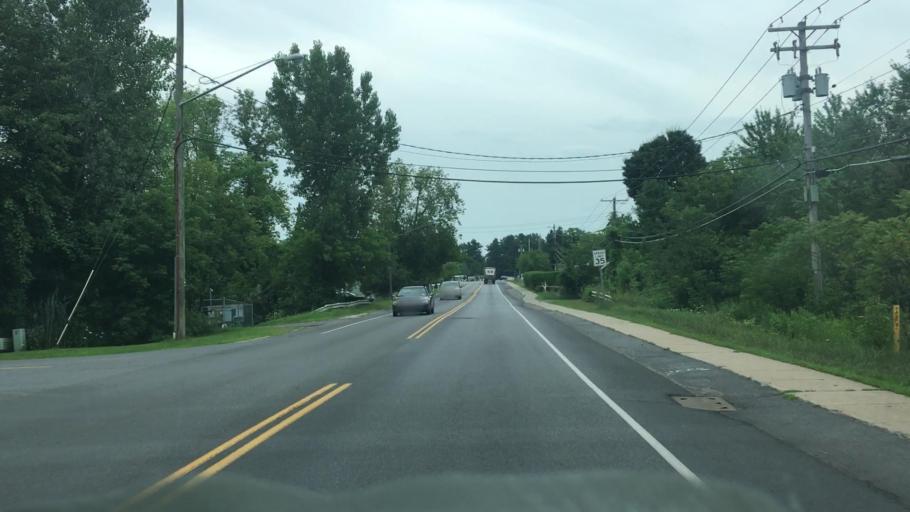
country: US
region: New York
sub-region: Clinton County
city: Plattsburgh West
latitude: 44.6788
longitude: -73.5058
